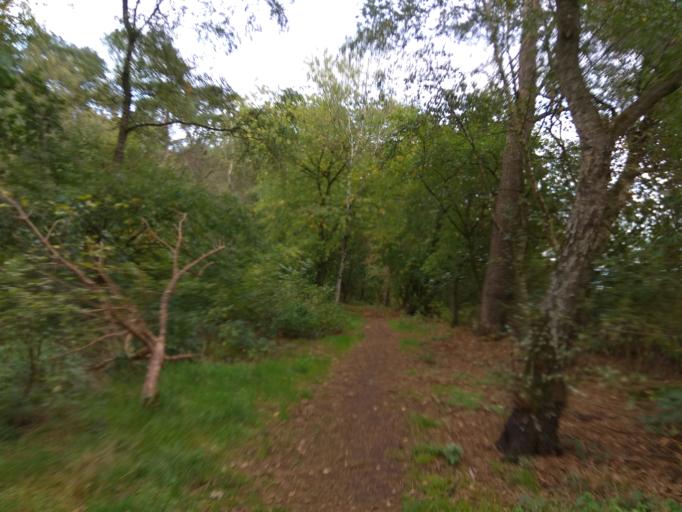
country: DE
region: North Rhine-Westphalia
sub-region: Regierungsbezirk Munster
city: Klein Reken
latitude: 51.7402
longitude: 7.0443
